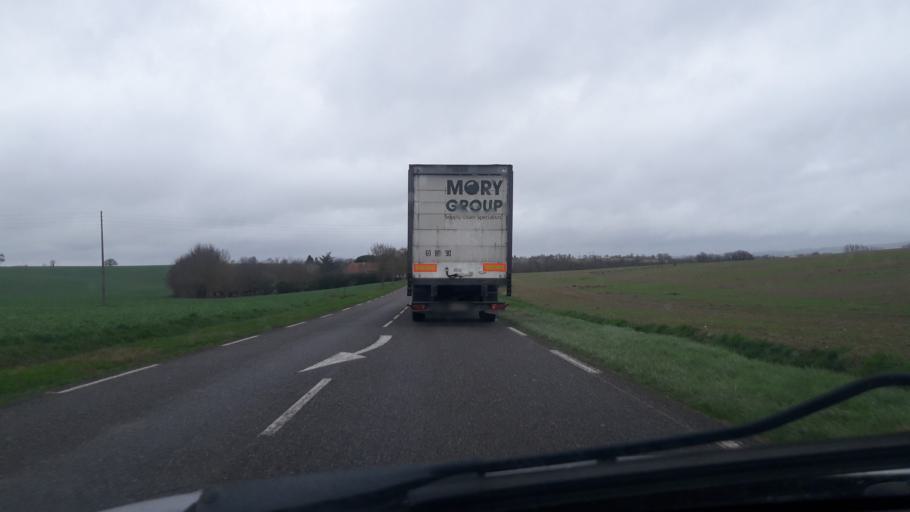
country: FR
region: Midi-Pyrenees
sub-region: Departement du Gers
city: Gimont
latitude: 43.7053
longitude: 0.9929
